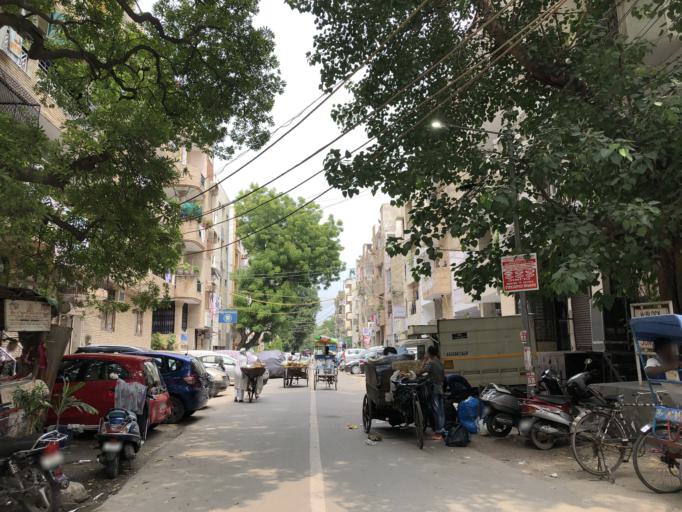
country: IN
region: NCT
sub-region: New Delhi
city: New Delhi
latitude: 28.5775
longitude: 77.2432
